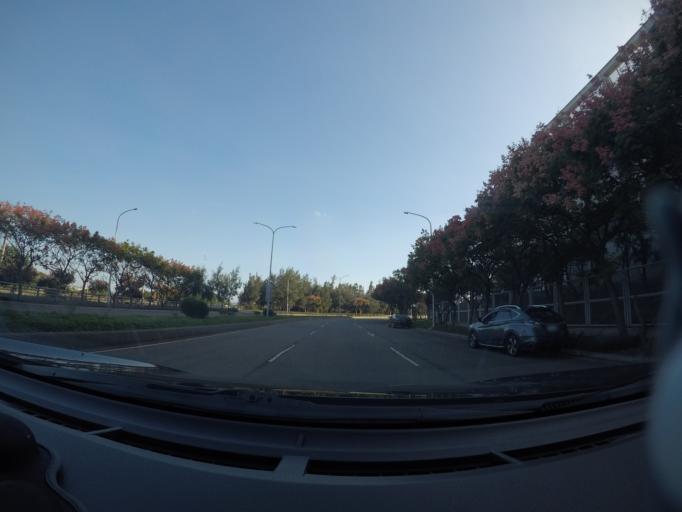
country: TW
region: Taiwan
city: Taoyuan City
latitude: 25.0950
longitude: 121.2574
